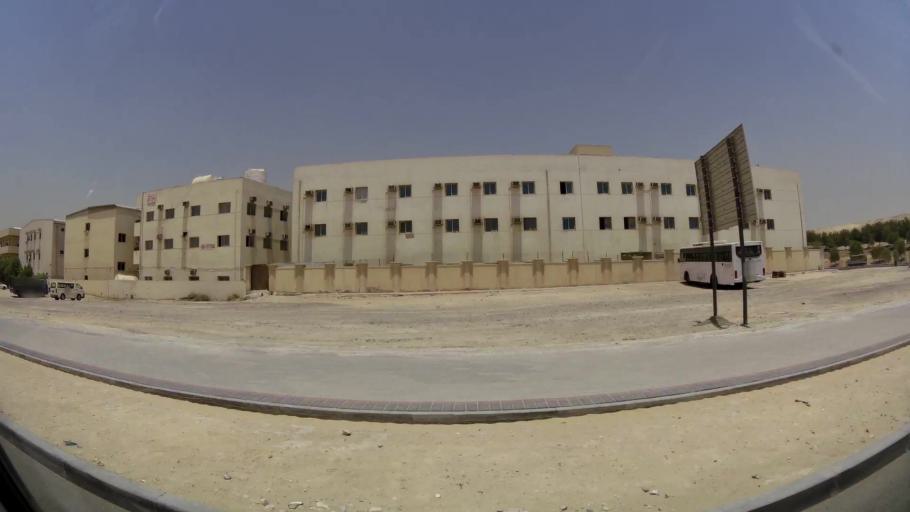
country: AE
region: Ash Shariqah
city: Sharjah
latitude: 25.2737
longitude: 55.4321
